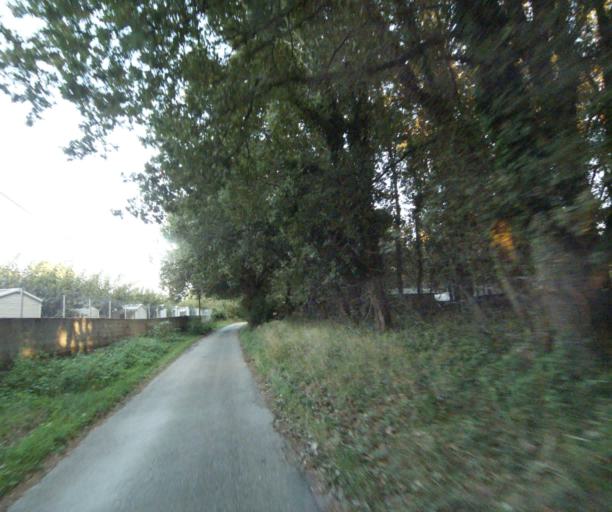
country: FR
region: Languedoc-Roussillon
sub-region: Departement des Pyrenees-Orientales
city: Argelers
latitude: 42.5737
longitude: 3.0127
